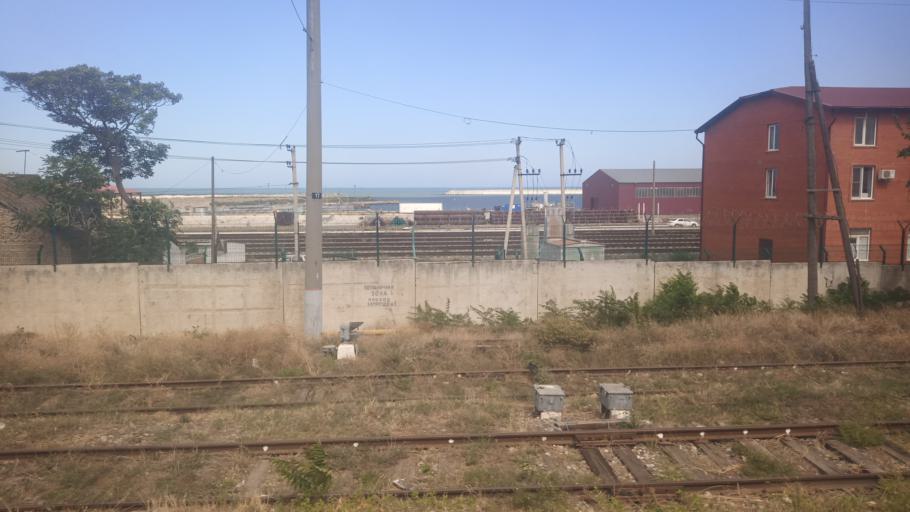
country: RU
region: Dagestan
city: Makhachkala
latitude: 42.9918
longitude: 47.4935
